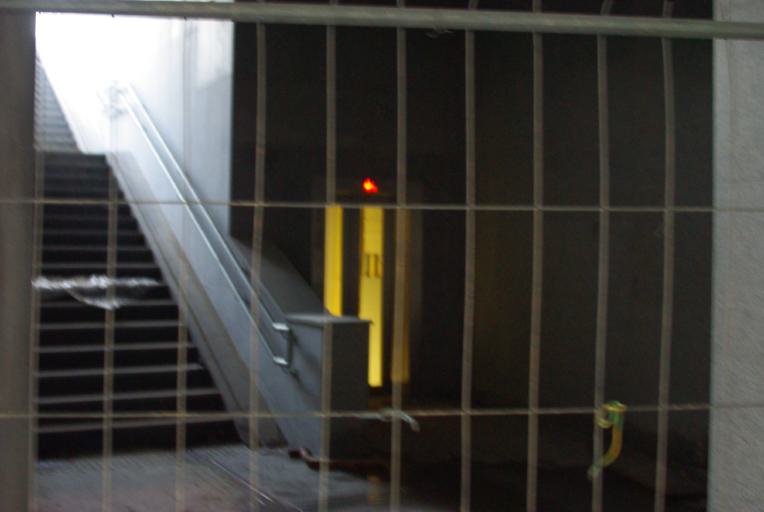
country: HU
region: Pest
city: Pilisszentivan
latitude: 47.6156
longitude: 18.8999
